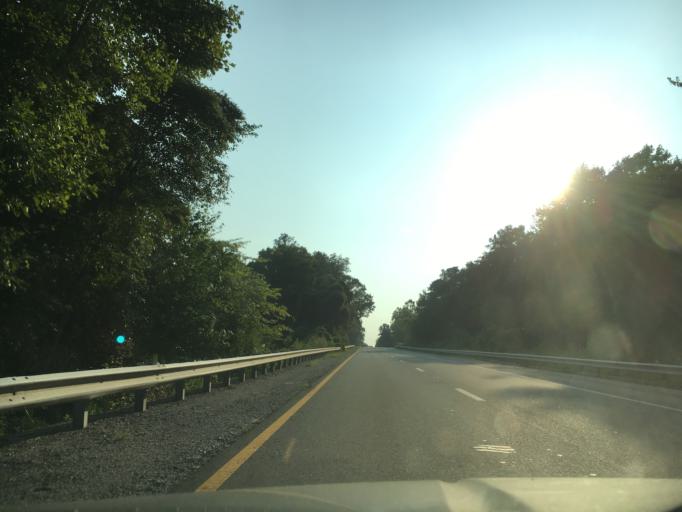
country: US
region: Virginia
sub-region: Prince Edward County
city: Hampden Sydney
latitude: 37.3126
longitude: -78.4932
